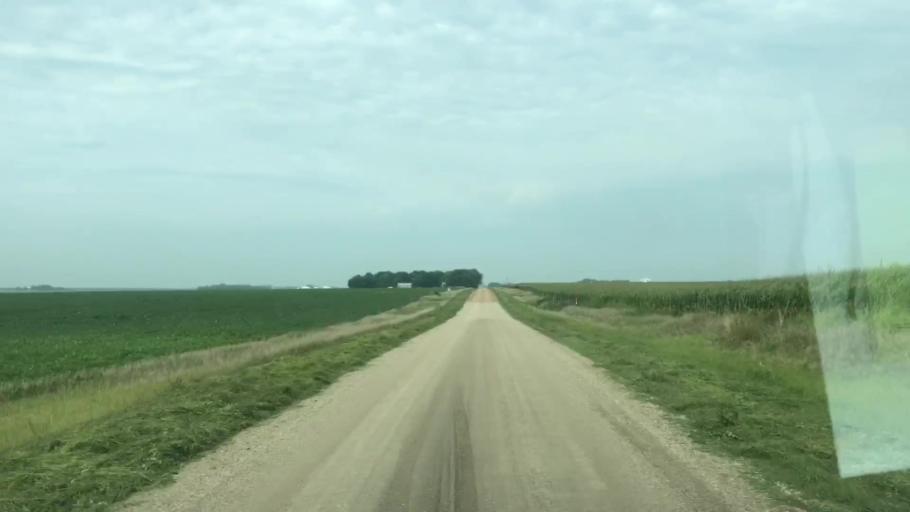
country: US
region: Iowa
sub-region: O'Brien County
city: Sheldon
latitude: 43.2721
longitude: -95.8653
